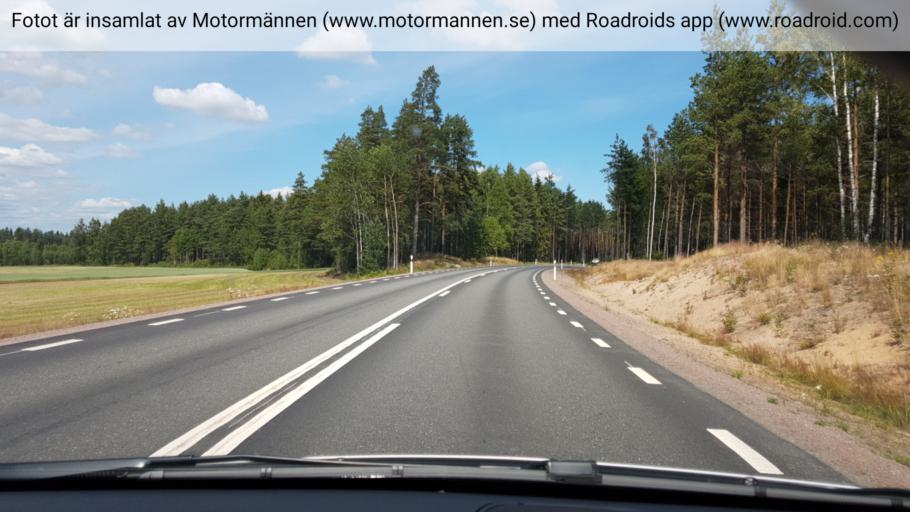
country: SE
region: Vaestra Goetaland
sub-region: Tibro Kommun
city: Tibro
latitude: 58.4570
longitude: 14.1771
